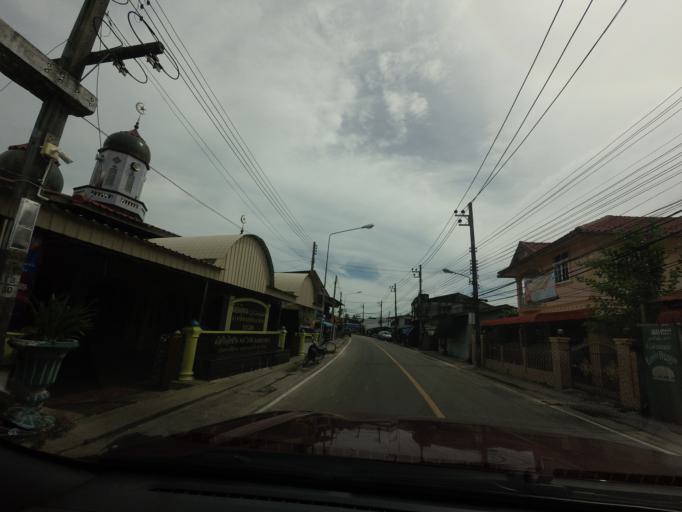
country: TH
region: Narathiwat
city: Tak Bai
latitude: 6.2358
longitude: 102.0880
